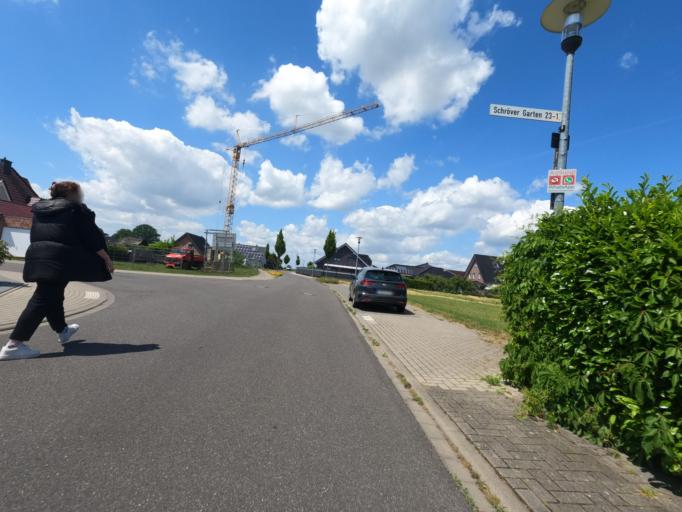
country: DE
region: North Rhine-Westphalia
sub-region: Regierungsbezirk Koln
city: Wassenberg
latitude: 51.0709
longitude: 6.1788
